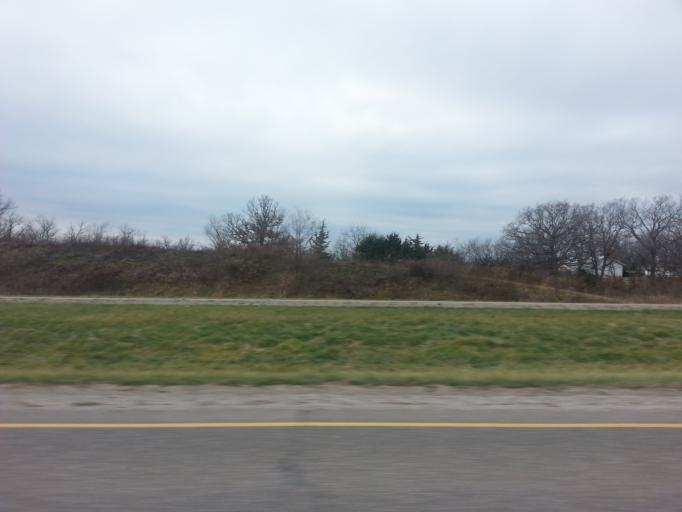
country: US
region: Iowa
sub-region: Henry County
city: Mount Pleasant
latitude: 40.9224
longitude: -91.5407
